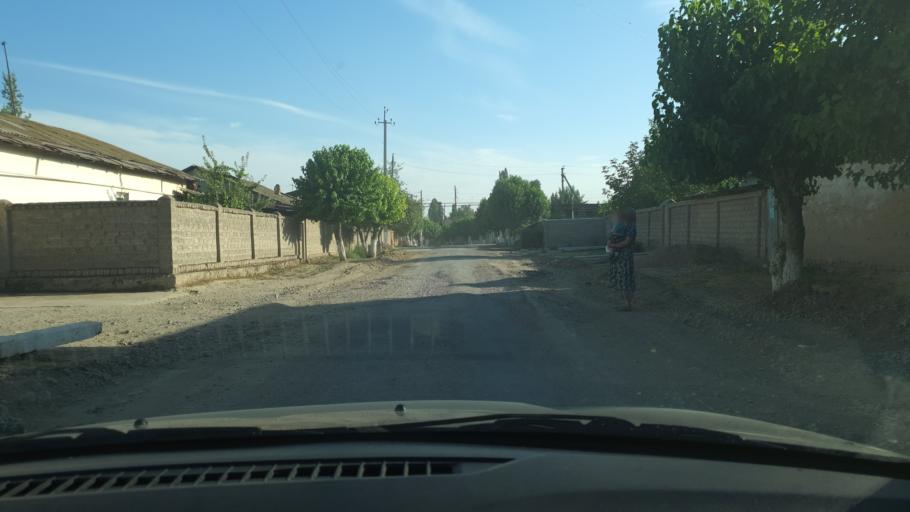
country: UZ
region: Toshkent
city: Tuytepa
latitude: 41.1036
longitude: 69.4020
